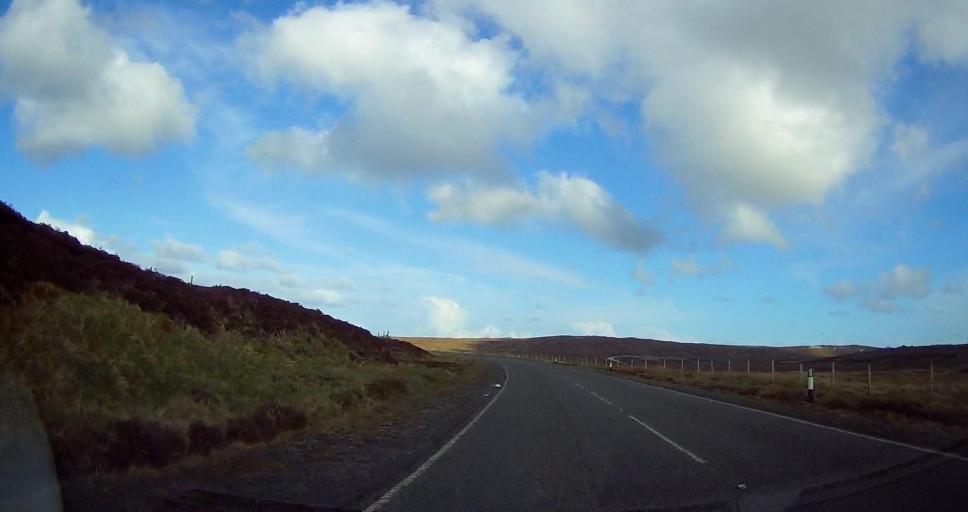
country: GB
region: Scotland
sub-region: Shetland Islands
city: Lerwick
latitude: 60.3490
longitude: -1.2296
